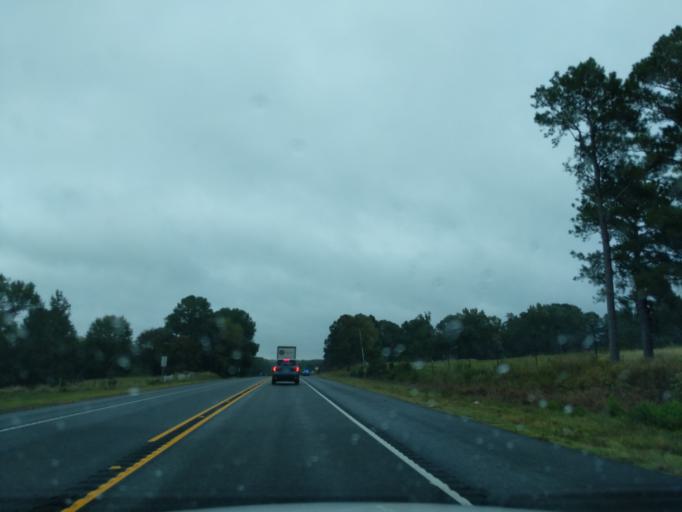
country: US
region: Louisiana
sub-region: Caddo Parish
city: Greenwood
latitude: 32.4365
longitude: -93.9835
